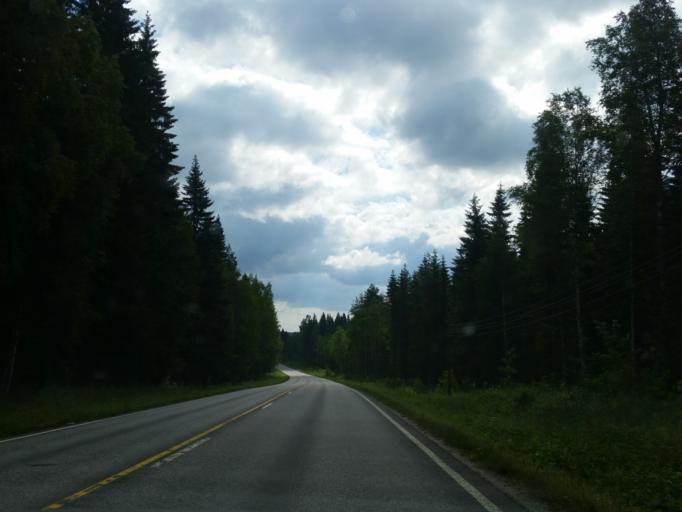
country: FI
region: Northern Savo
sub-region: Kuopio
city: Kuopio
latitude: 62.8455
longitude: 27.4047
